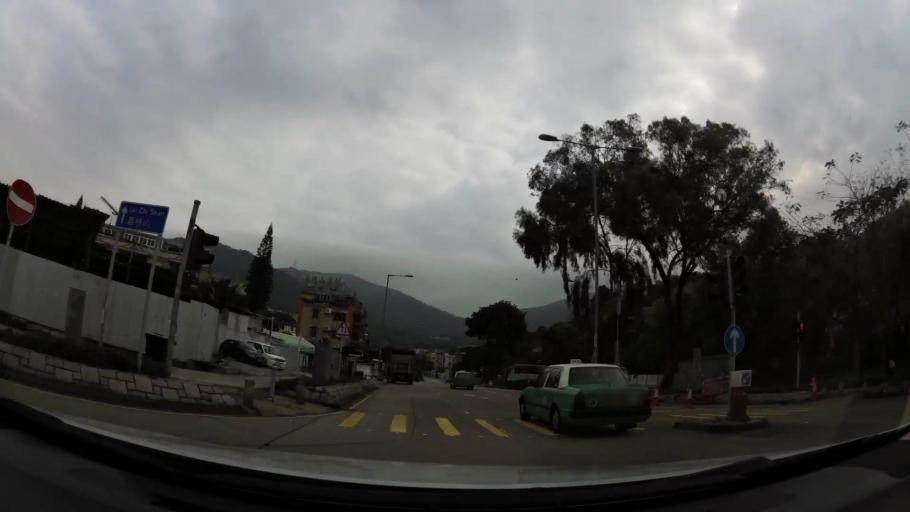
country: HK
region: Tai Po
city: Tai Po
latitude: 22.4385
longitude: 114.1648
